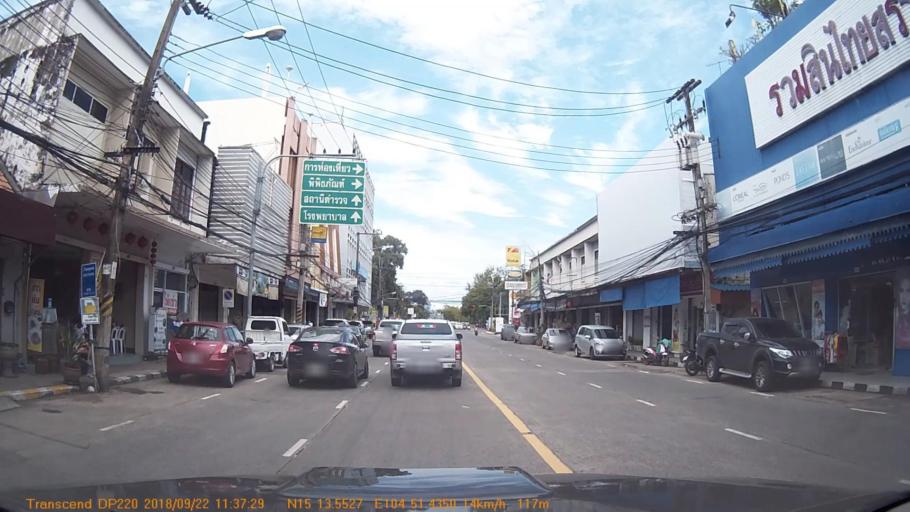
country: TH
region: Changwat Ubon Ratchathani
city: Ubon Ratchathani
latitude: 15.2259
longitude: 104.8572
